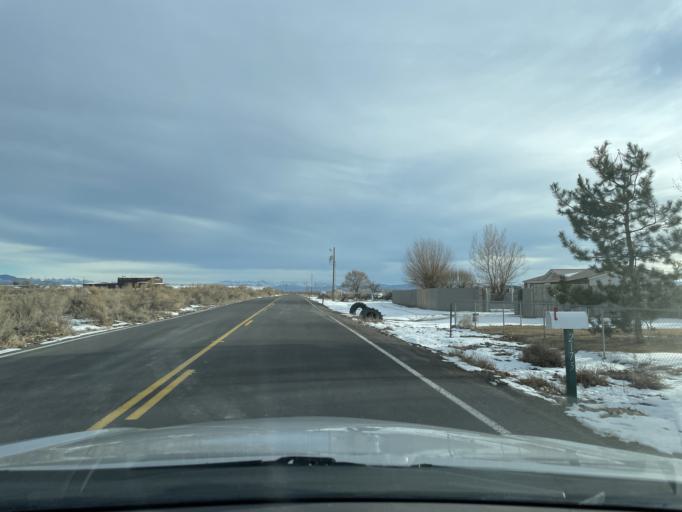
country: US
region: Colorado
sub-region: Montrose County
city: Olathe
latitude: 38.6617
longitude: -107.9984
